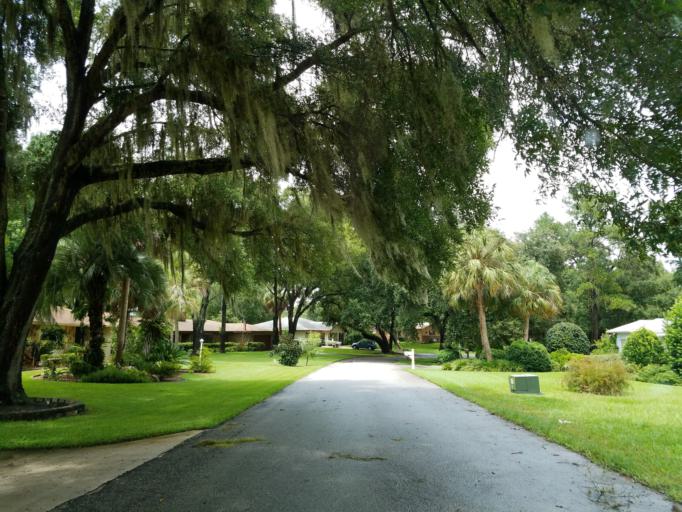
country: US
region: Florida
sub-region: Citrus County
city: Inverness
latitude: 28.8189
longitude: -82.2912
